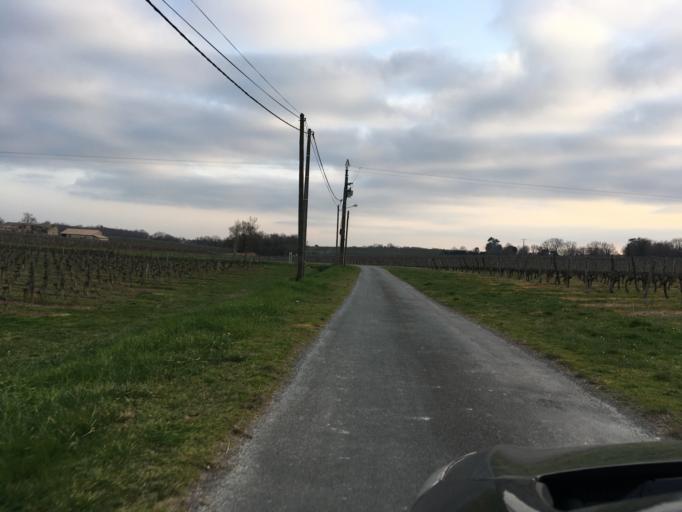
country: FR
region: Aquitaine
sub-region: Departement de la Gironde
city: Saint-Ciers-sur-Gironde
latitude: 45.3134
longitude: -0.6031
